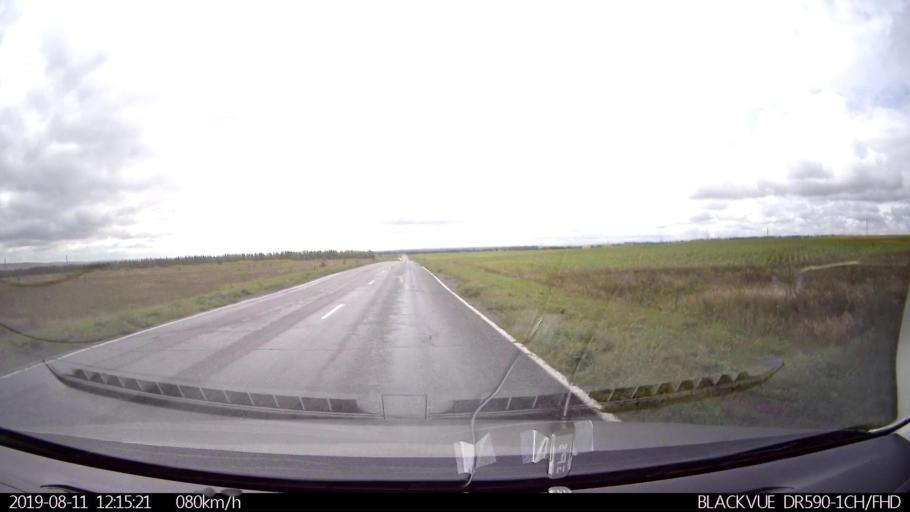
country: RU
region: Ulyanovsk
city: Ignatovka
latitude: 53.9427
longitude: 47.9694
